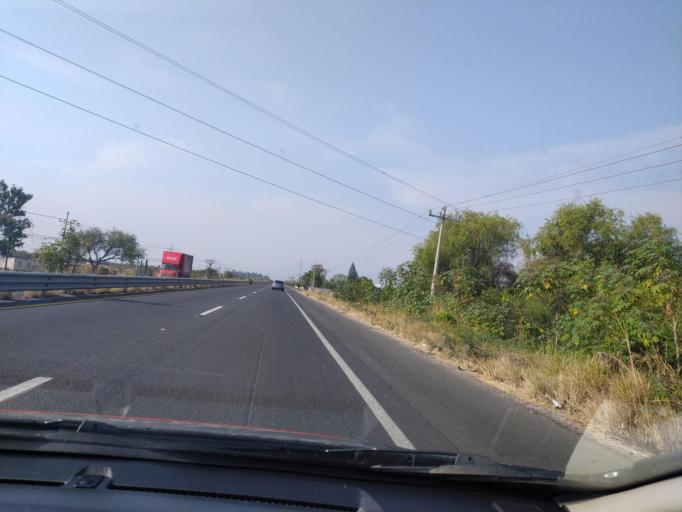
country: MX
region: Jalisco
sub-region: Acatlan de Juarez
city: Villa de los Ninos
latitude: 20.3862
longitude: -103.5931
